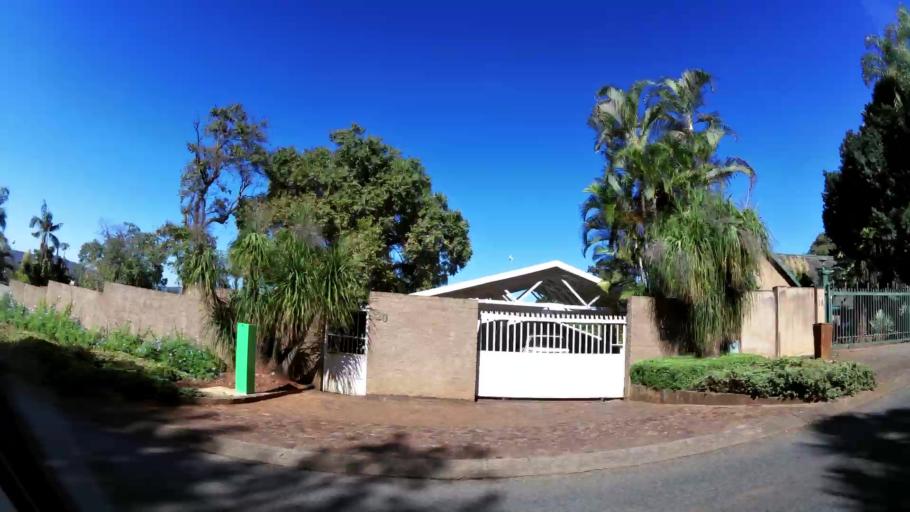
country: ZA
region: Limpopo
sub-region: Mopani District Municipality
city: Tzaneen
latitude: -23.8270
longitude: 30.1470
